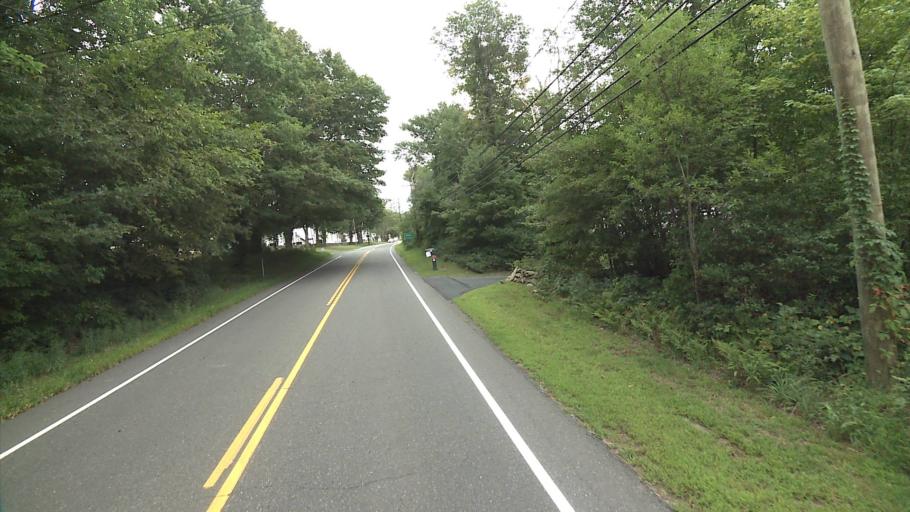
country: US
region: Connecticut
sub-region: New London County
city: Colchester
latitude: 41.4938
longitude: -72.2778
